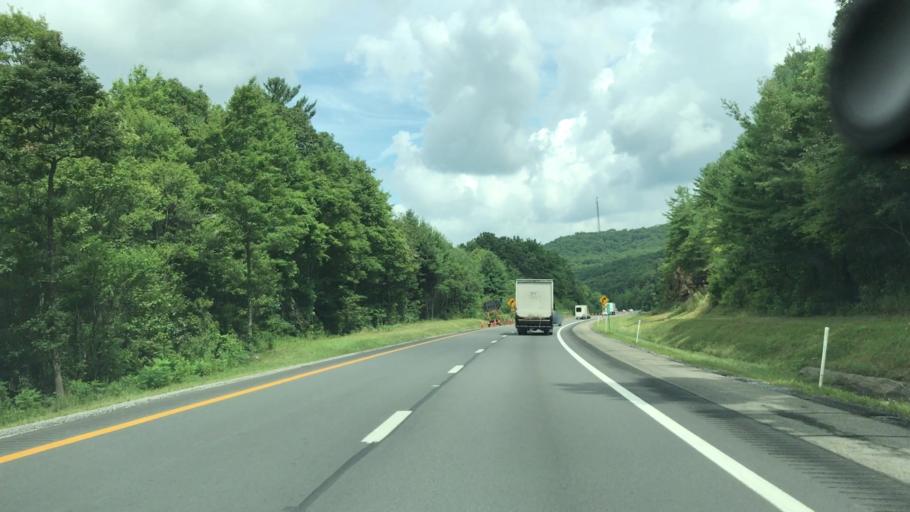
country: US
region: West Virginia
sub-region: Raleigh County
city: Shady Spring
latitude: 37.6885
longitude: -81.1286
